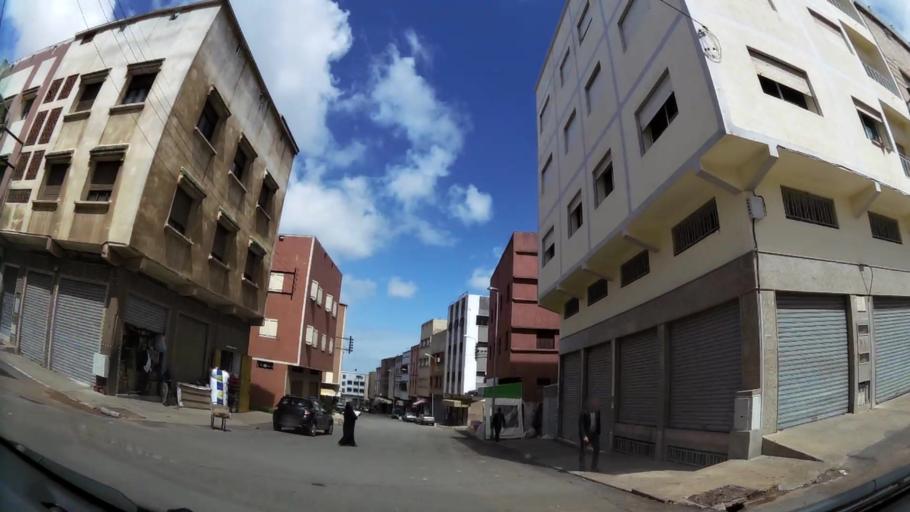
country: MA
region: Grand Casablanca
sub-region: Casablanca
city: Casablanca
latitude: 33.5359
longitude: -7.5849
